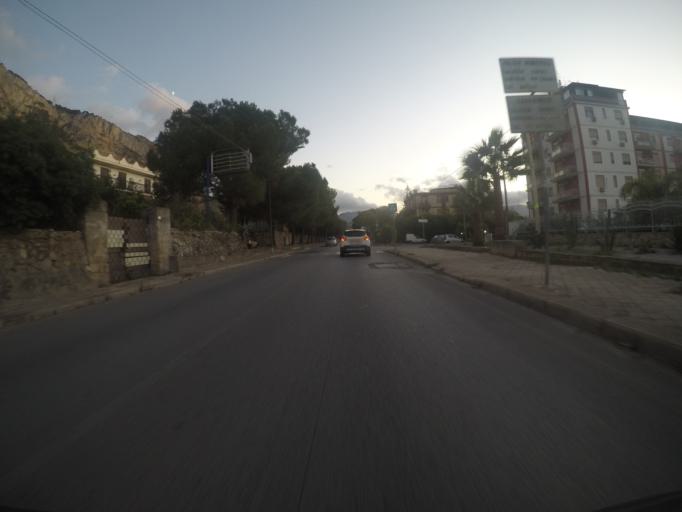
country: IT
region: Sicily
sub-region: Palermo
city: Capaci
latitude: 38.1788
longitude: 13.2442
